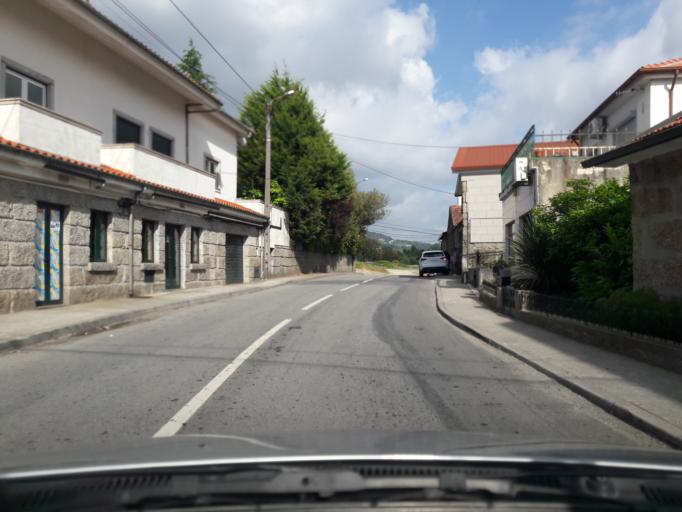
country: PT
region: Braga
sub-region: Guimaraes
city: Candoso
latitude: 41.4215
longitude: -8.3156
